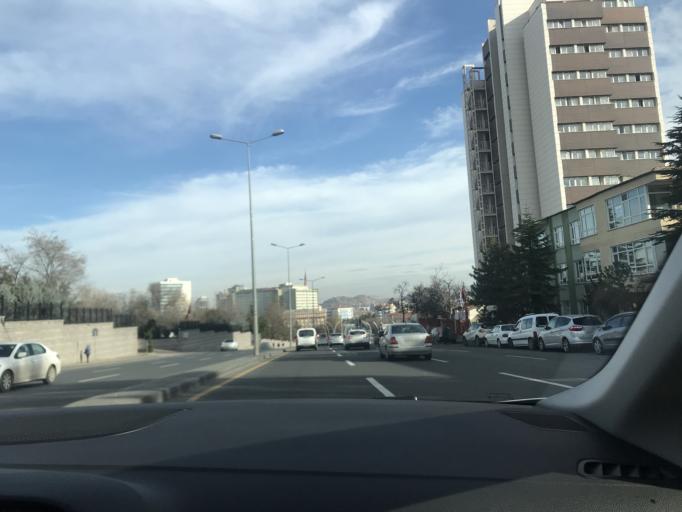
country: TR
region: Ankara
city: Ankara
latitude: 39.9306
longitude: 32.8165
